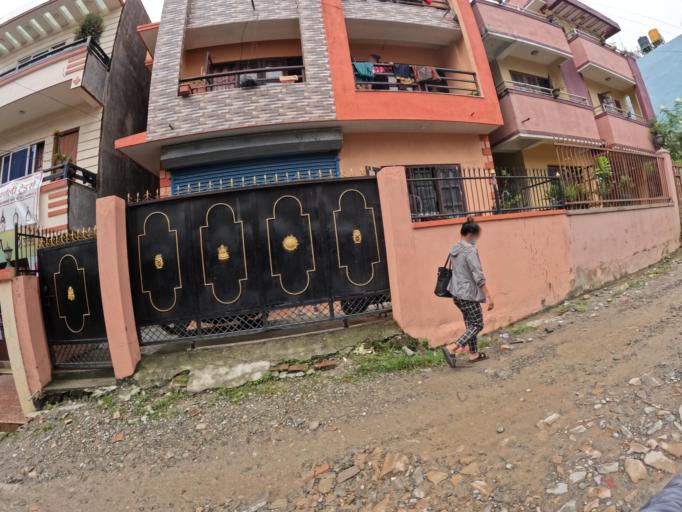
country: NP
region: Central Region
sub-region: Bagmati Zone
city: Kathmandu
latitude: 27.7556
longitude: 85.3231
